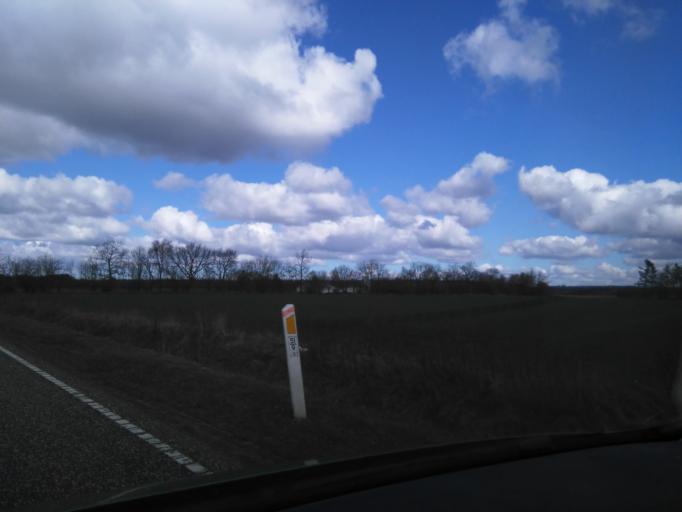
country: DK
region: Central Jutland
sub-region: Ikast-Brande Kommune
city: Bording Kirkeby
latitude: 56.1123
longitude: 9.3578
